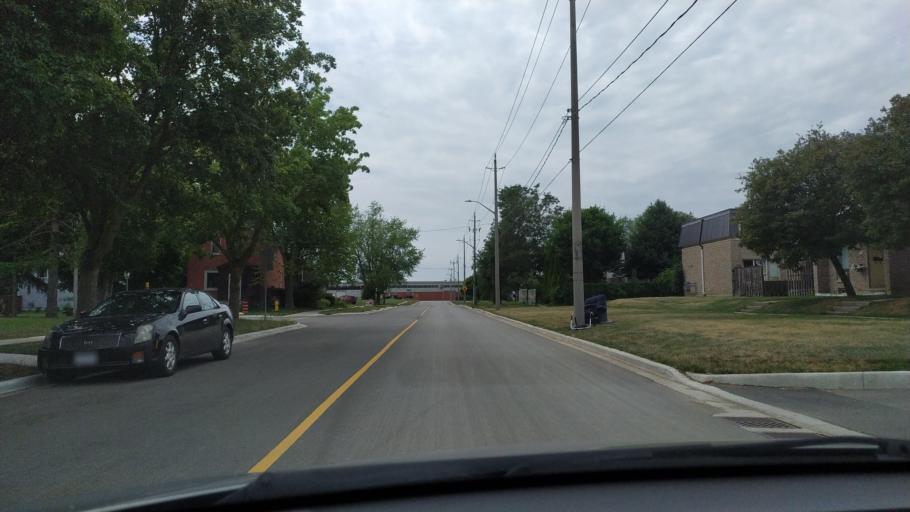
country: CA
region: Ontario
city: Stratford
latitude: 43.3605
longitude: -80.9999
